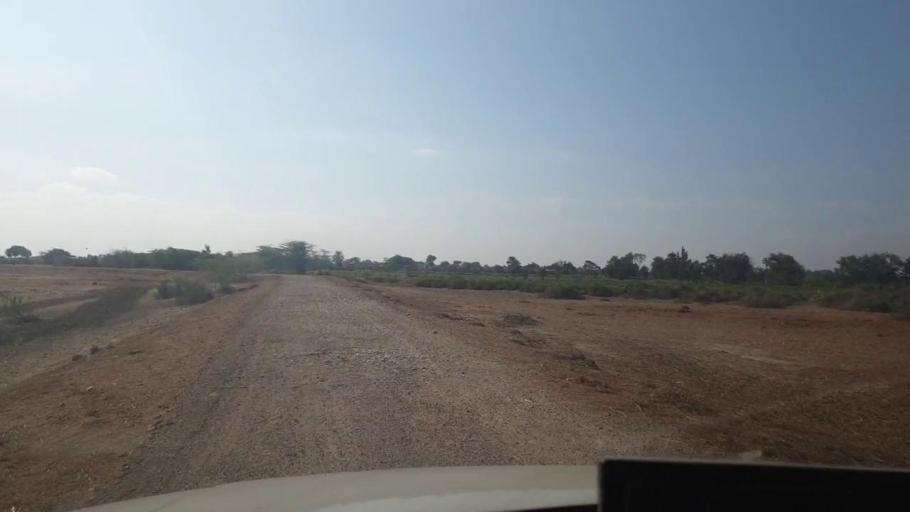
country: PK
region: Sindh
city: Mirpur Sakro
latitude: 24.4689
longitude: 67.5953
